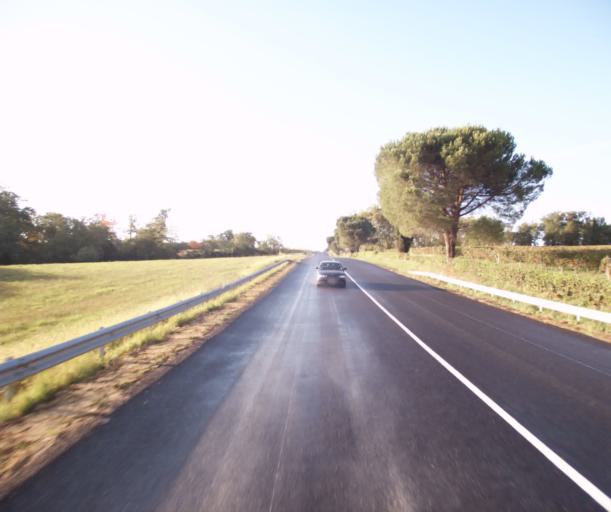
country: FR
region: Midi-Pyrenees
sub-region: Departement du Gers
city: Cazaubon
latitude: 43.9124
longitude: -0.0245
